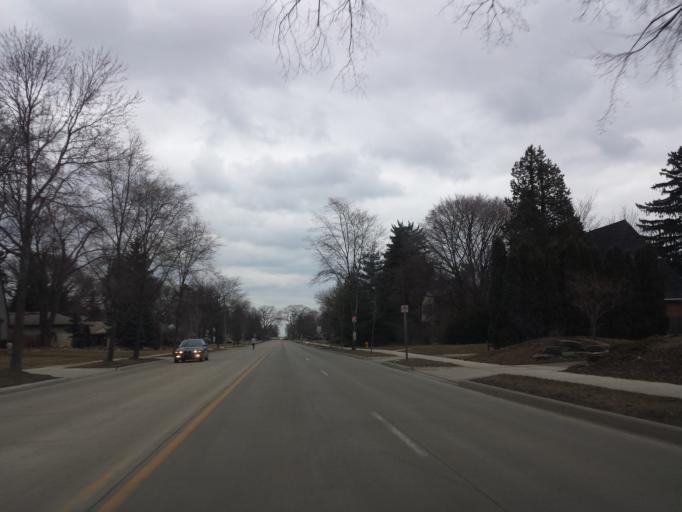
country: US
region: Michigan
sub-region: Oakland County
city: Birmingham
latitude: 42.5470
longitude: -83.2038
